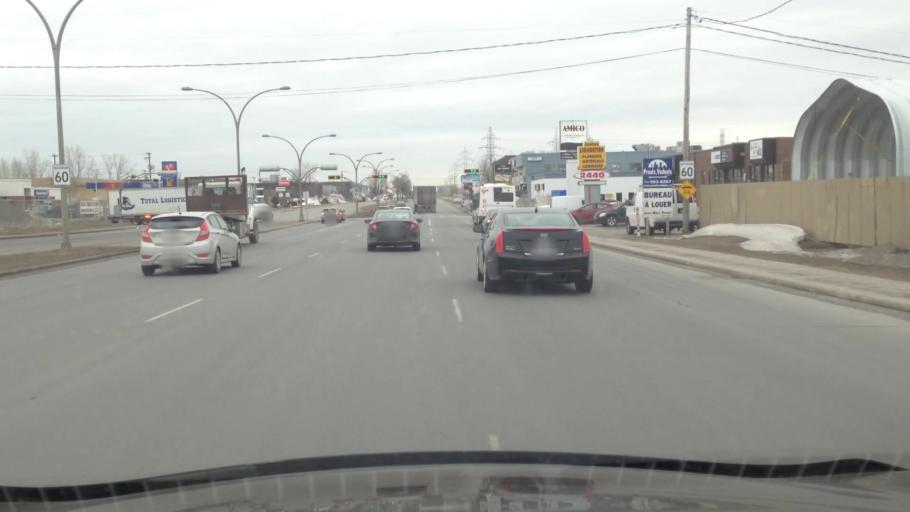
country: CA
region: Quebec
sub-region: Laval
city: Laval
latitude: 45.5827
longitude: -73.7337
